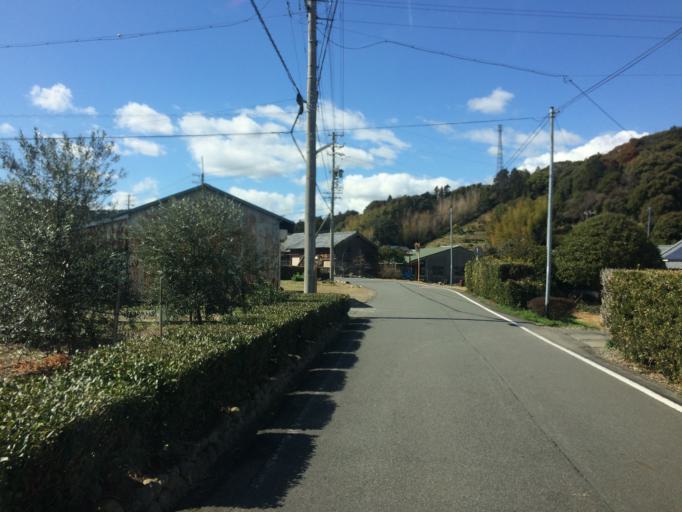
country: JP
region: Shizuoka
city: Shimada
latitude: 34.7576
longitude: 138.1883
